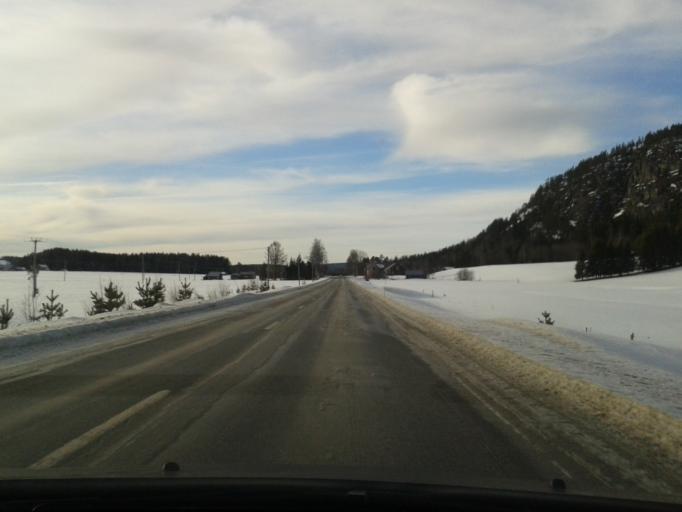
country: SE
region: Vaesternorrland
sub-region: OErnskoeldsviks Kommun
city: Bredbyn
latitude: 63.5269
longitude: 18.0153
